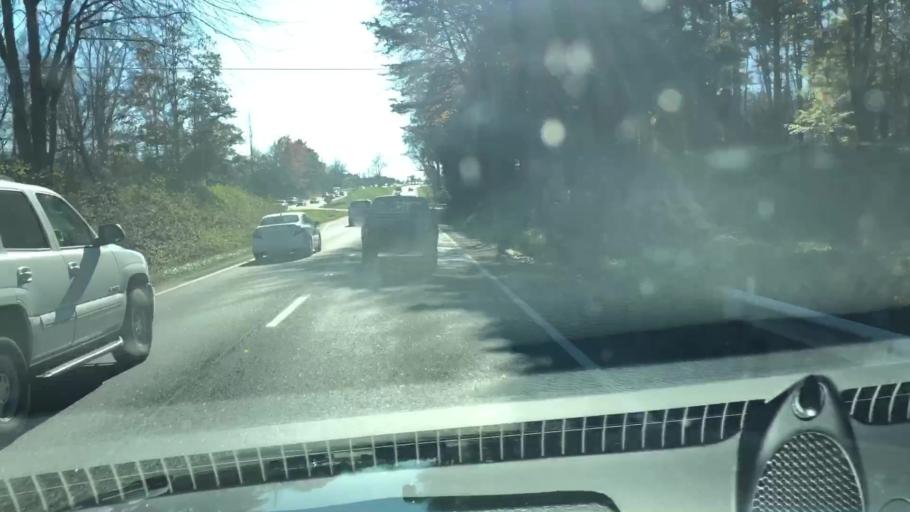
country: US
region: Virginia
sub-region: Albemarle County
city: Hollymead
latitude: 38.1375
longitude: -78.4317
